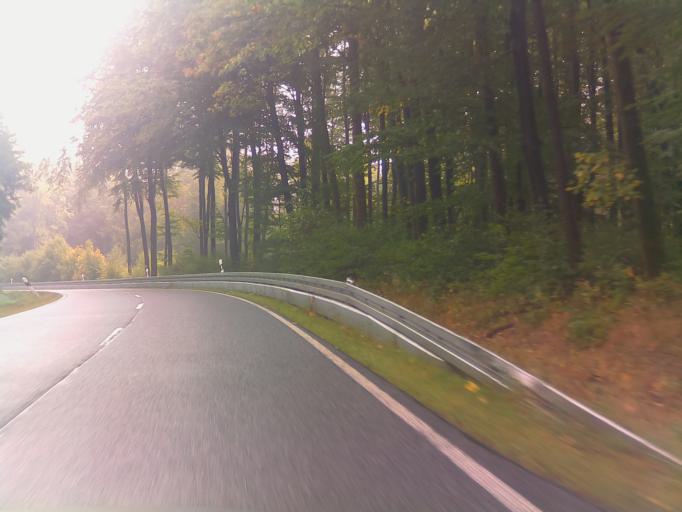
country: DE
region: Hesse
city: Gedern
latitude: 50.4549
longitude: 9.2538
